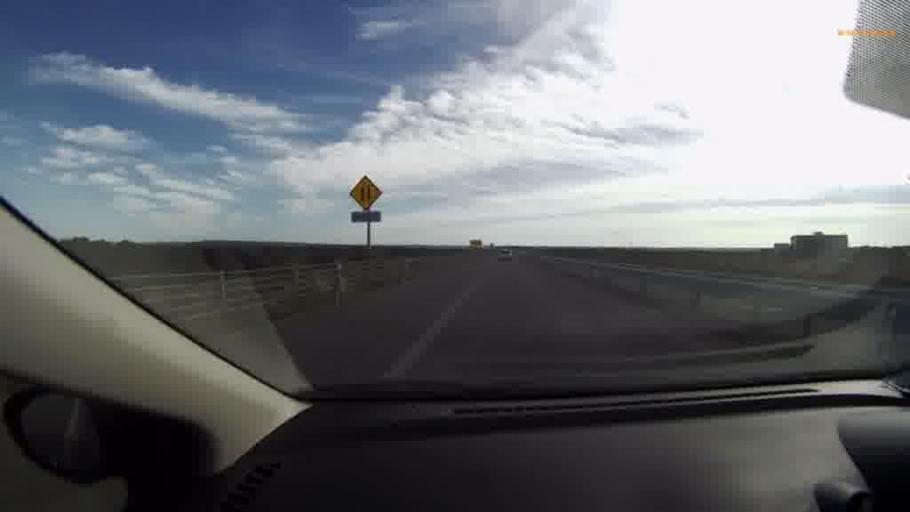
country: JP
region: Hokkaido
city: Kushiro
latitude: 43.0370
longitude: 144.3528
